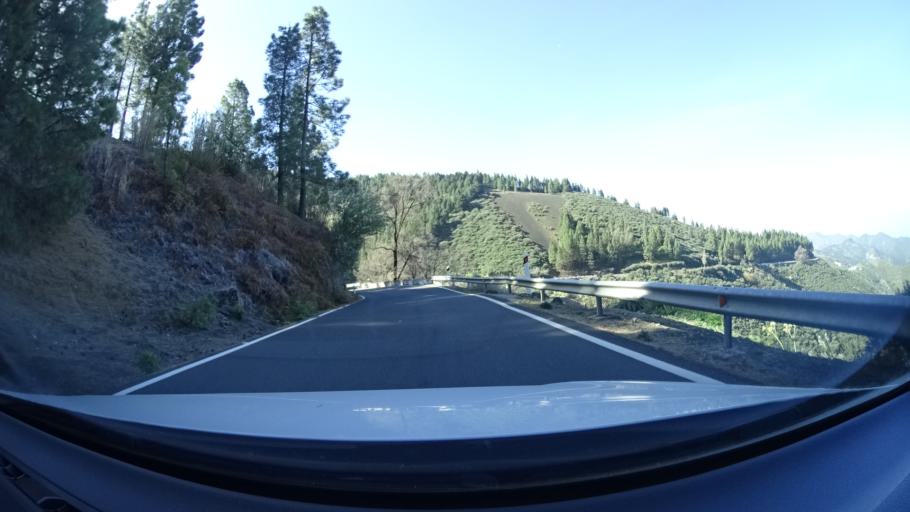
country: ES
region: Canary Islands
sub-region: Provincia de Las Palmas
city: Artenara
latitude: 28.0285
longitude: -15.6181
